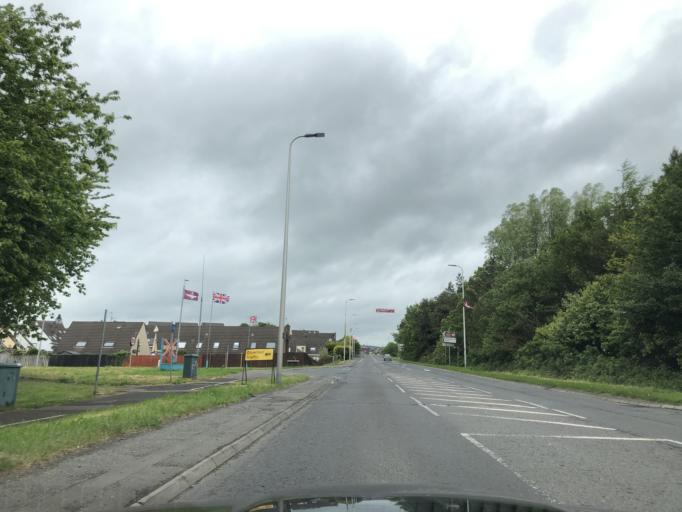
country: GB
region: Northern Ireland
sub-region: Lisburn District
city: Lisburn
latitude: 54.5254
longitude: -6.0732
